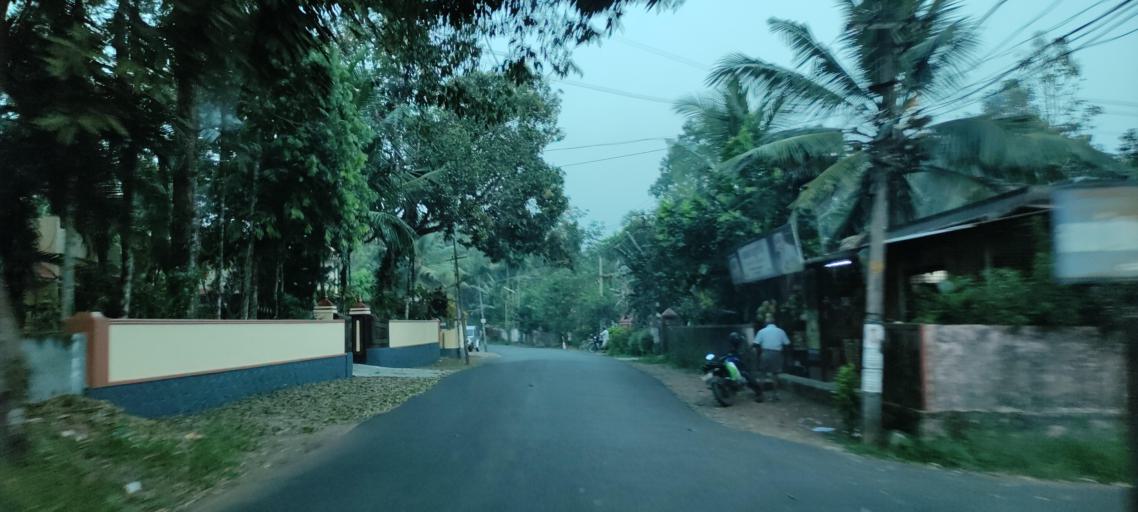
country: IN
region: Kerala
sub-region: Pattanamtitta
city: Adur
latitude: 9.1587
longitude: 76.7521
